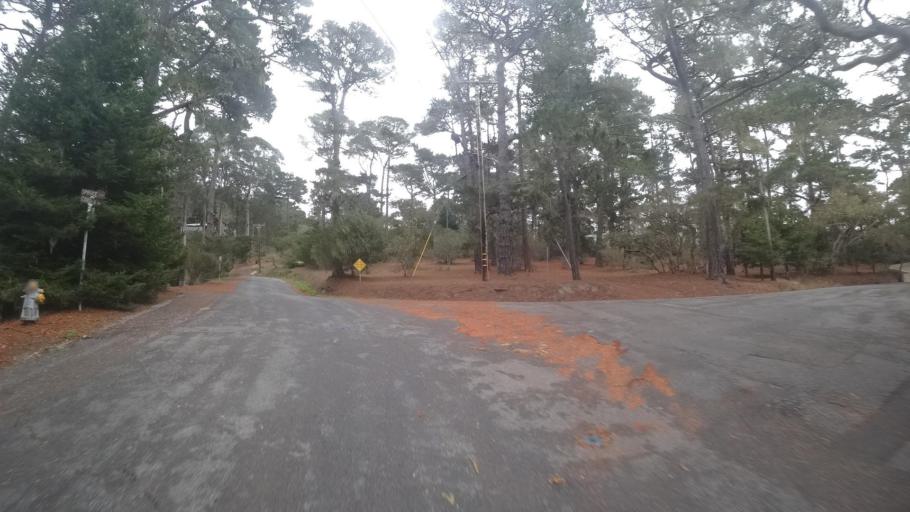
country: US
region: California
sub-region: Monterey County
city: Carmel-by-the-Sea
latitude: 36.5068
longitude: -121.9310
